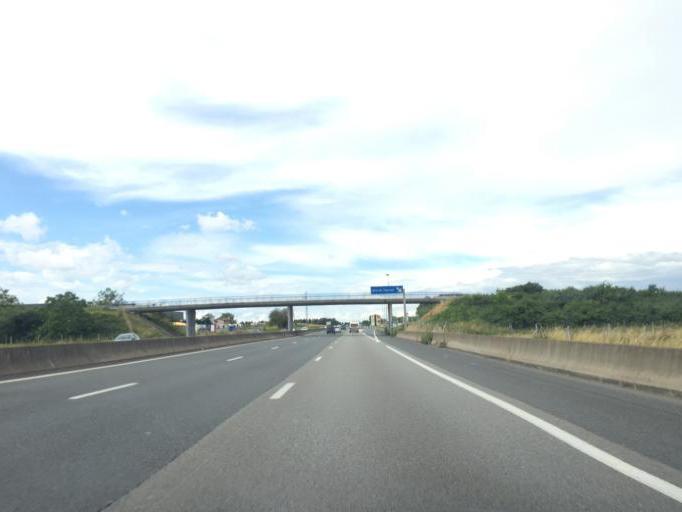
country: FR
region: Rhone-Alpes
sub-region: Departement de l'Ain
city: Guereins
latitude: 46.1304
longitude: 4.7655
